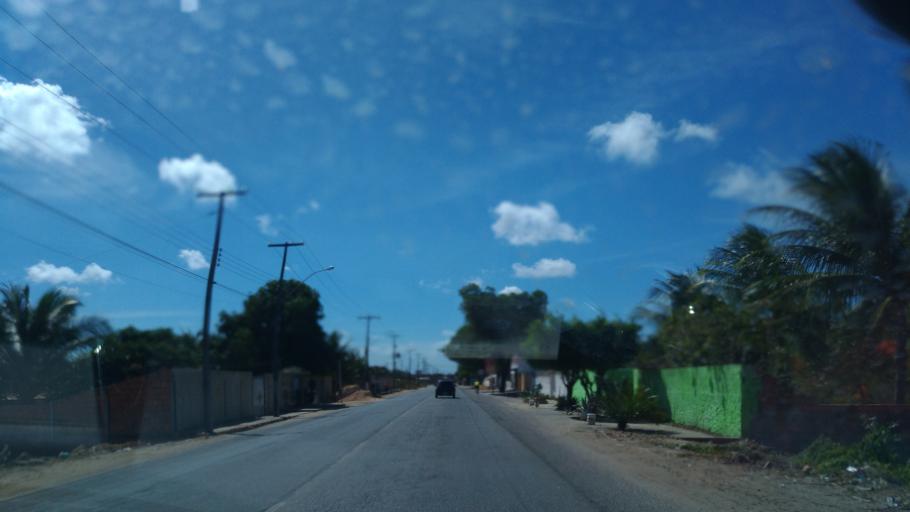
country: BR
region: Alagoas
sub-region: Marechal Deodoro
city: Marechal Deodoro
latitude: -9.7629
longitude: -35.8610
